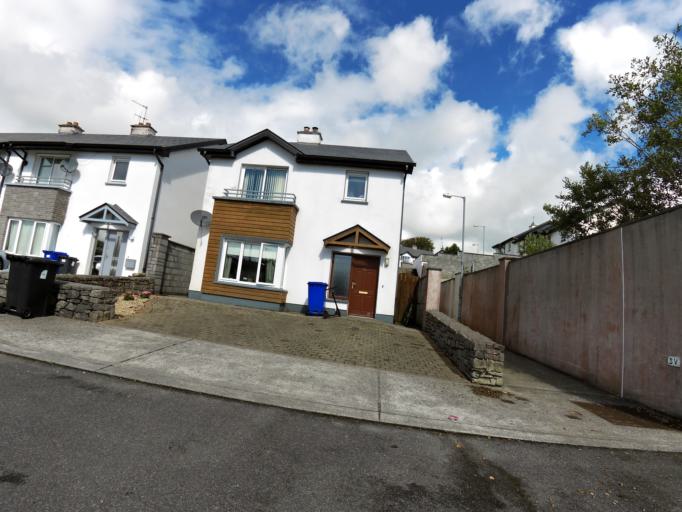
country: IE
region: Connaught
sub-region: County Galway
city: Loughrea
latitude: 53.1955
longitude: -8.5557
